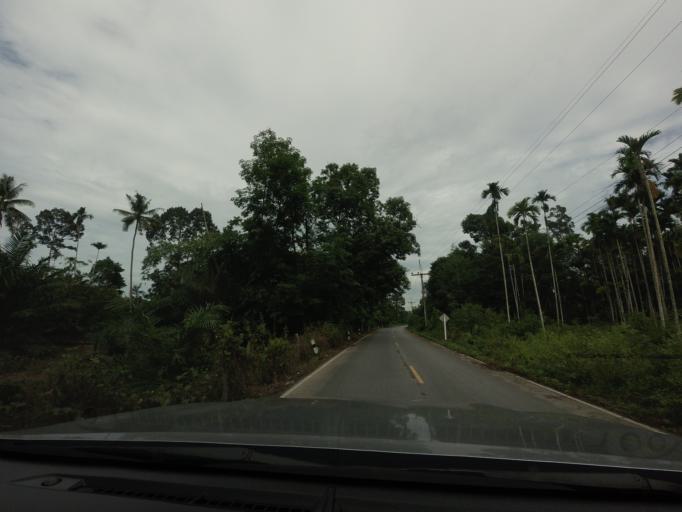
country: TH
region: Nakhon Si Thammarat
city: Phra Phrom
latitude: 8.2828
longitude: 99.9280
